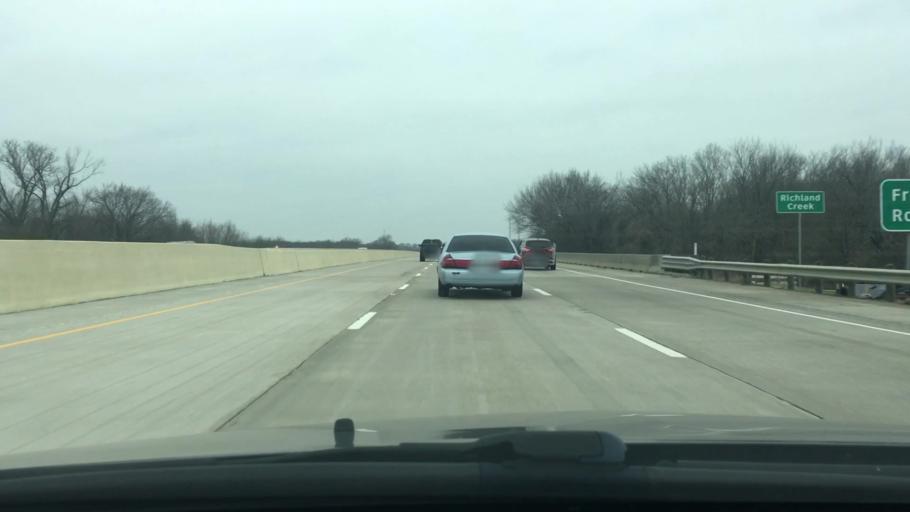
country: US
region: Texas
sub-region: Navarro County
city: Corsicana
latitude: 31.9509
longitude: -96.4217
